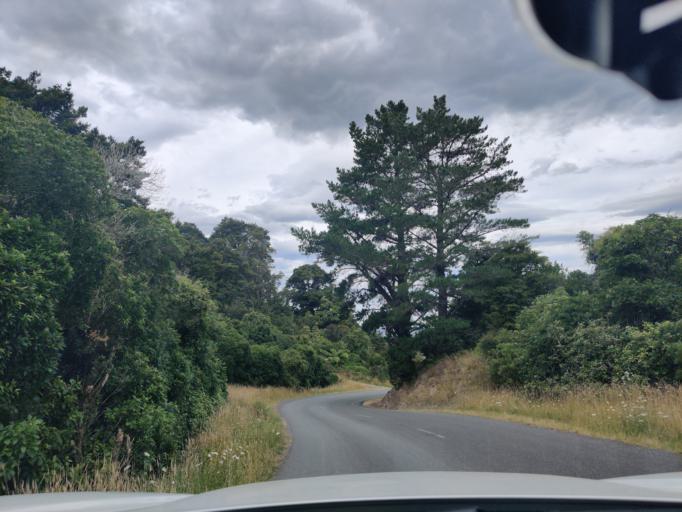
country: NZ
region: Wellington
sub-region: Masterton District
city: Masterton
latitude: -41.0367
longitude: 175.4185
